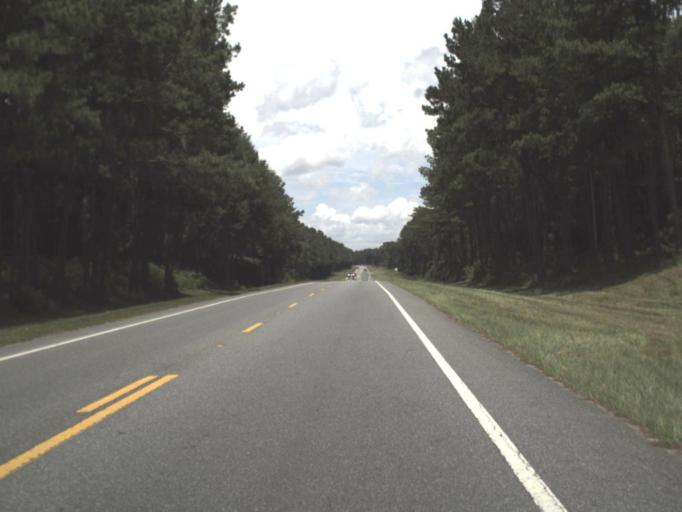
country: US
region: Florida
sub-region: Suwannee County
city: Live Oak
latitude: 30.3413
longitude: -82.9547
